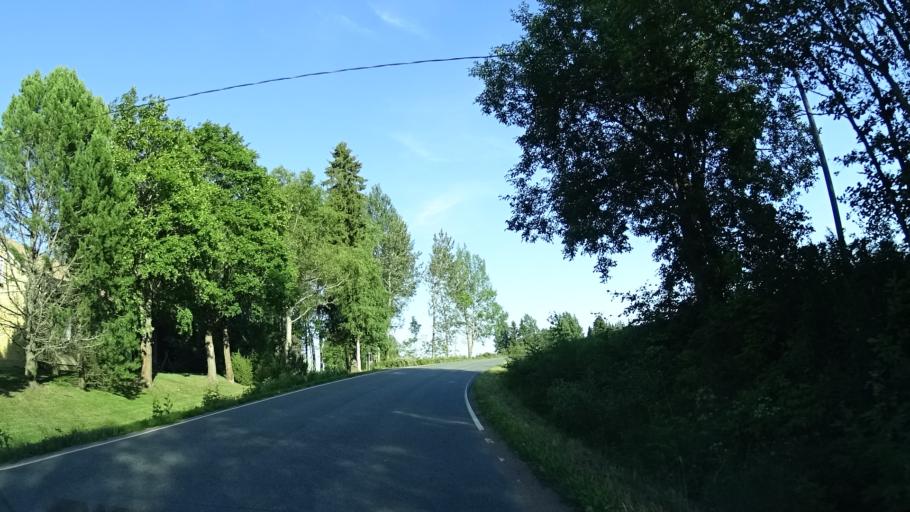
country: FI
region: Satakunta
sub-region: Pori
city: Kokemaeki
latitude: 61.2698
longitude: 22.3004
